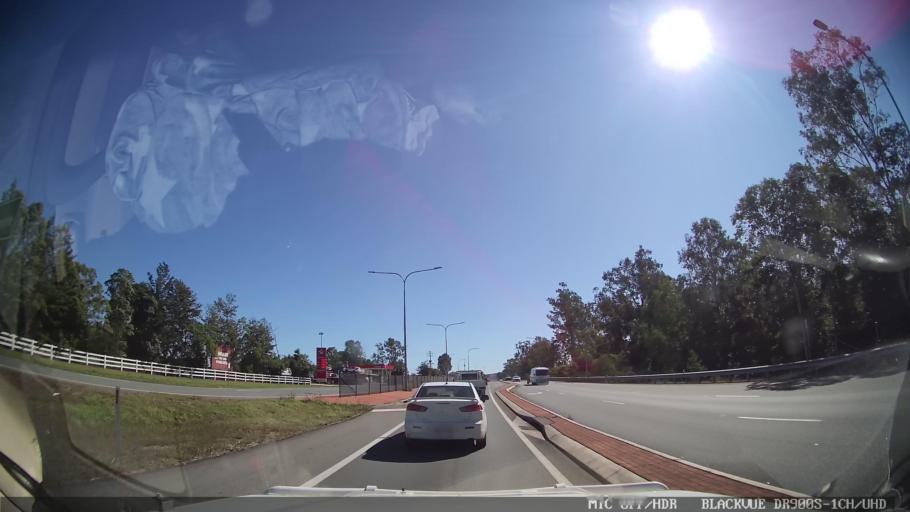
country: AU
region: Queensland
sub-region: Gympie Regional Council
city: Monkland
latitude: -26.2395
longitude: 152.6999
